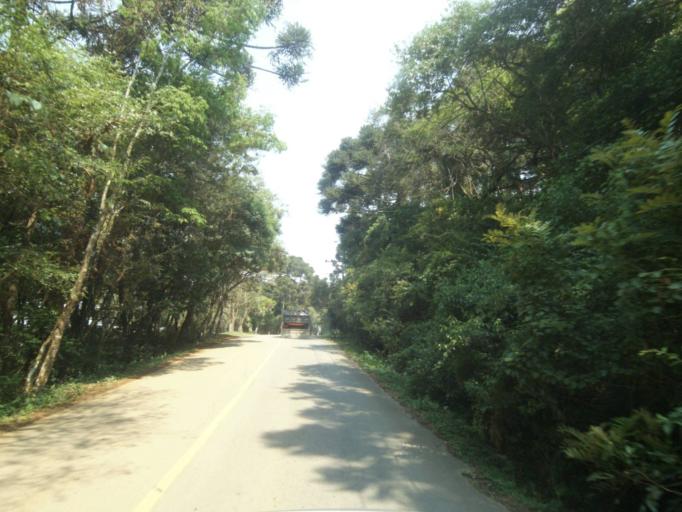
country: BR
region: Parana
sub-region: Sao Jose Dos Pinhais
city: Sao Jose dos Pinhais
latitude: -25.5492
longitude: -49.2366
